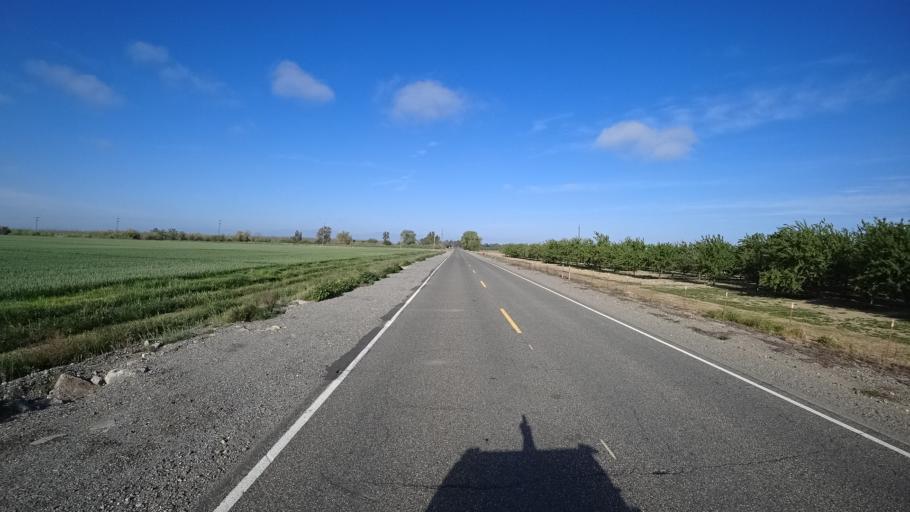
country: US
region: California
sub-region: Glenn County
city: Willows
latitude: 39.5823
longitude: -122.1726
